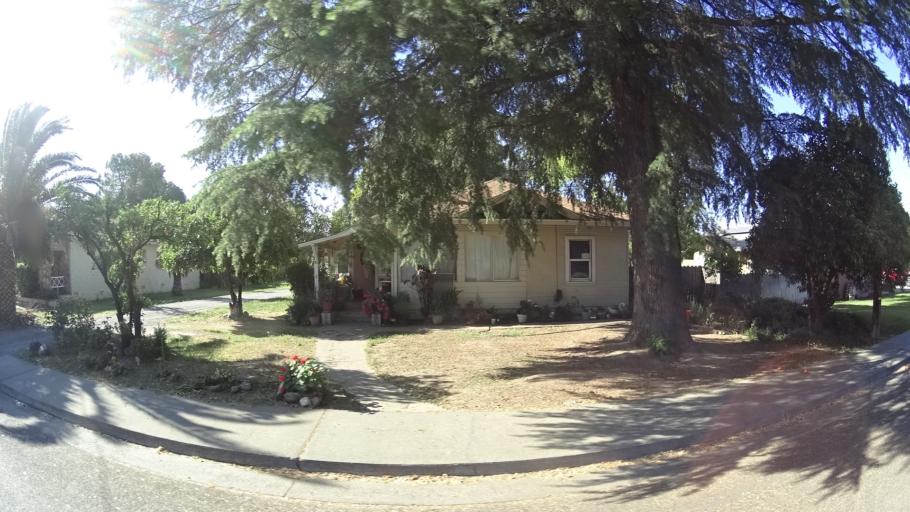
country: US
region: California
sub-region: Glenn County
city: Orland
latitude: 39.7426
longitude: -122.1892
